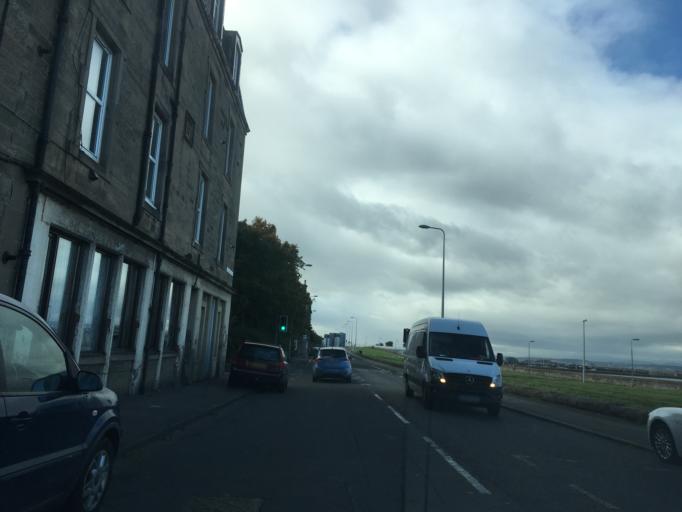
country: GB
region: Scotland
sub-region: Edinburgh
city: Edinburgh
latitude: 55.9800
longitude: -3.2076
